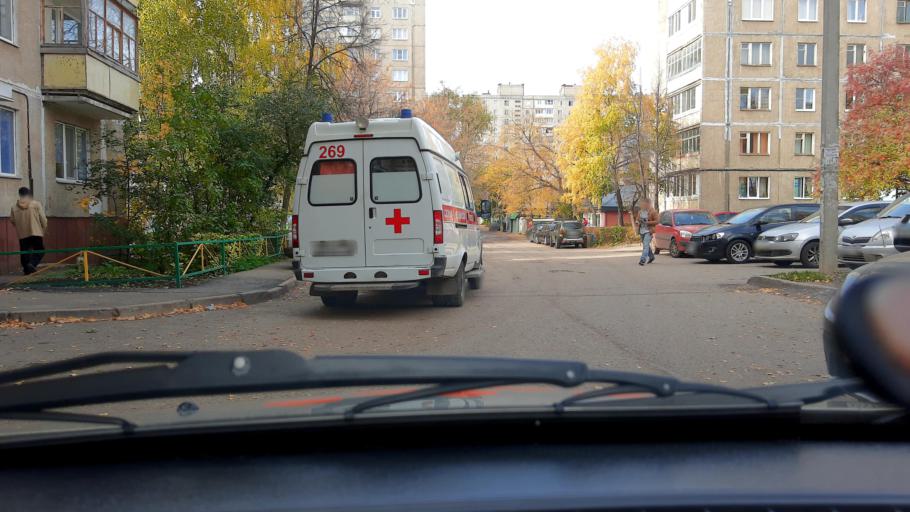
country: RU
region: Bashkortostan
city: Ufa
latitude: 54.7055
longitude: 56.0056
